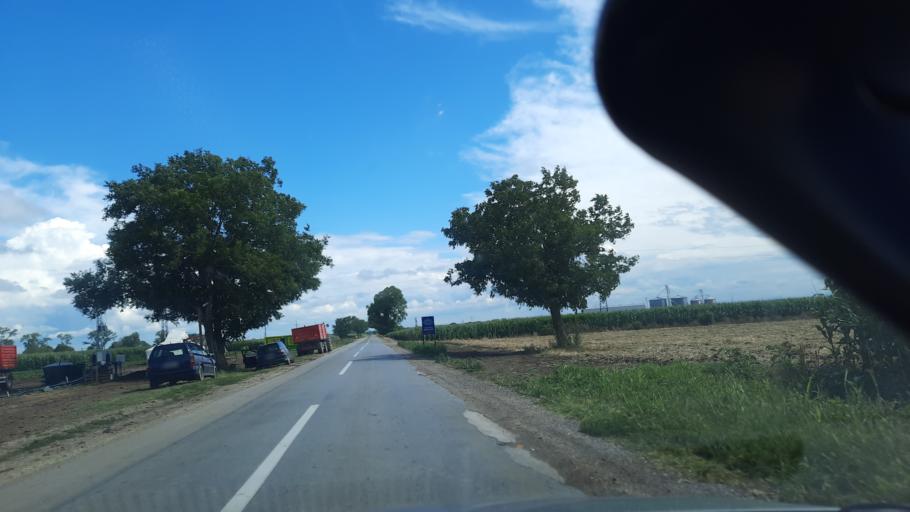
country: RS
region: Autonomna Pokrajina Vojvodina
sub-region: Sremski Okrug
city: Sremska Mitrovica
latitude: 45.0510
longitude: 19.6034
